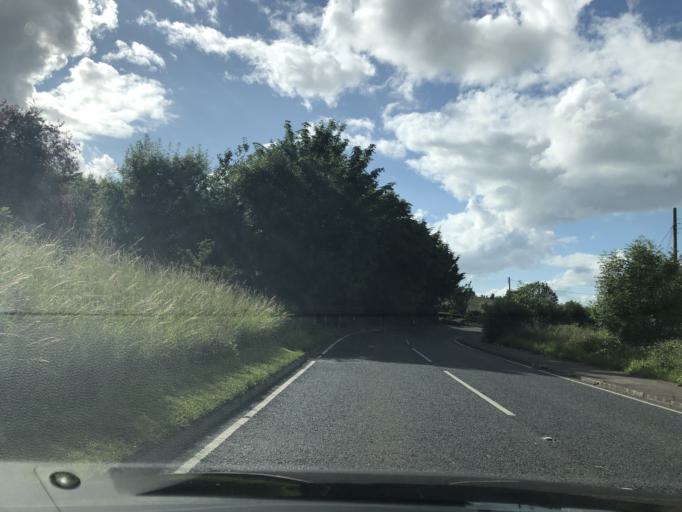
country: GB
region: Northern Ireland
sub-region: Castlereagh District
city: Dundonald
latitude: 54.5786
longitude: -5.7893
